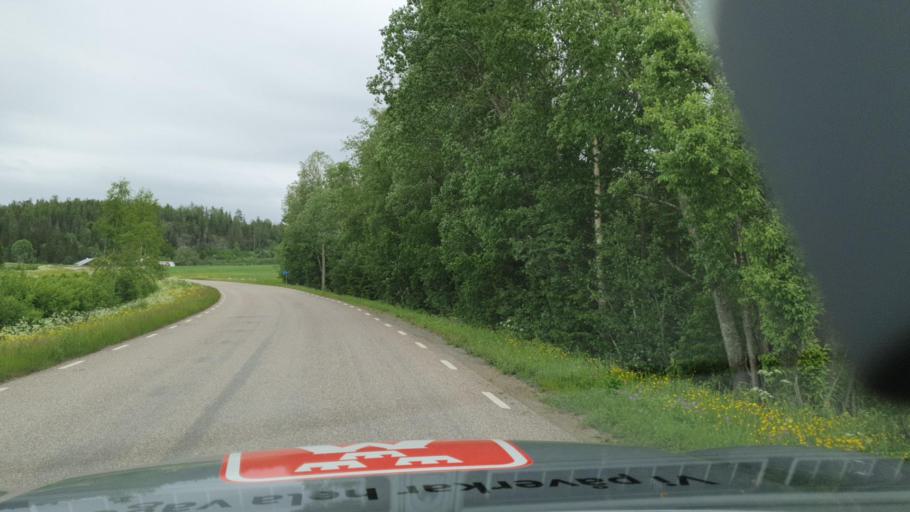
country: SE
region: Vaesternorrland
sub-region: Kramfors Kommun
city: Nordingra
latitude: 62.9024
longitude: 18.3607
